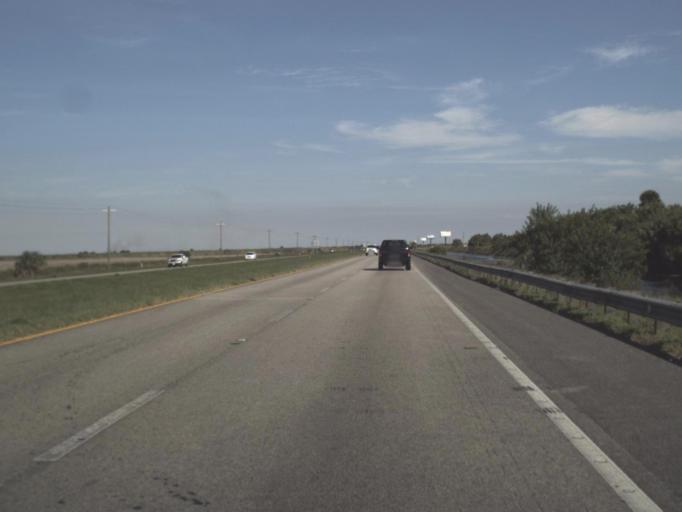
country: US
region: Florida
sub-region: Glades County
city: Moore Haven
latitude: 26.7535
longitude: -81.0710
